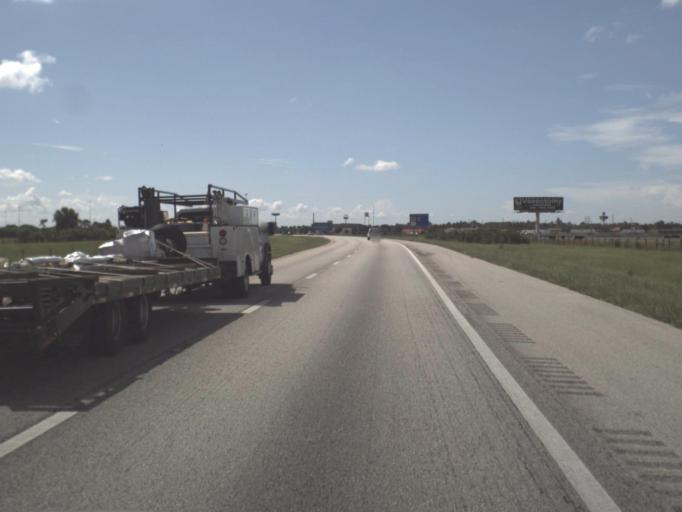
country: US
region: Florida
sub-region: Charlotte County
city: Punta Gorda
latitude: 26.9041
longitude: -82.0087
